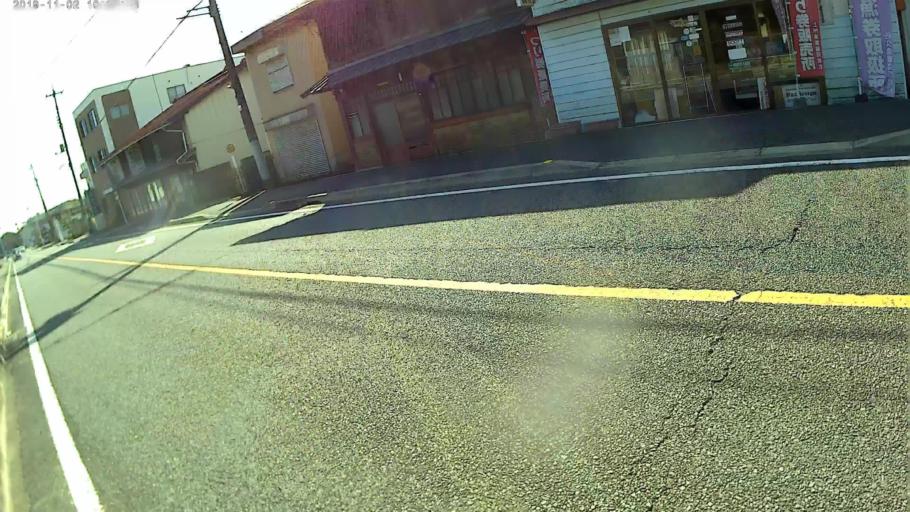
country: JP
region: Gunma
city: Annaka
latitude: 36.3124
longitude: 138.8031
